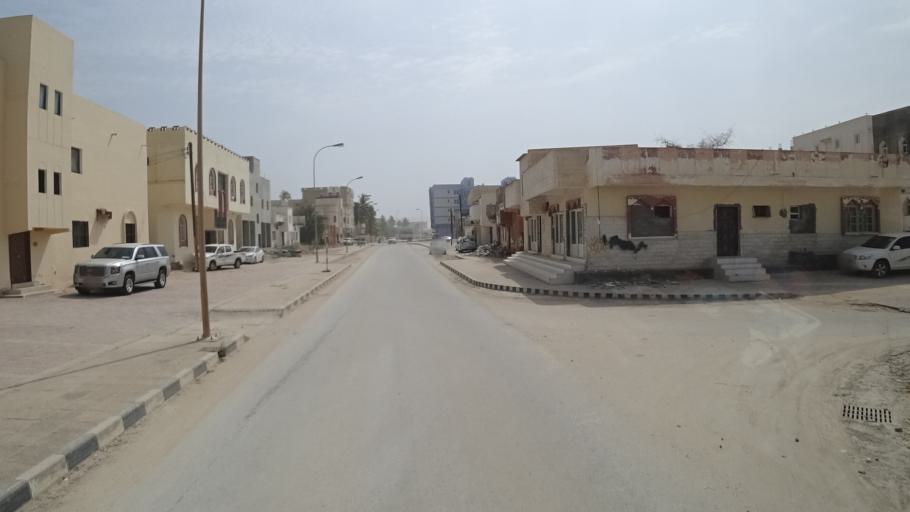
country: OM
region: Zufar
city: Salalah
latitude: 17.0096
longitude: 54.1590
